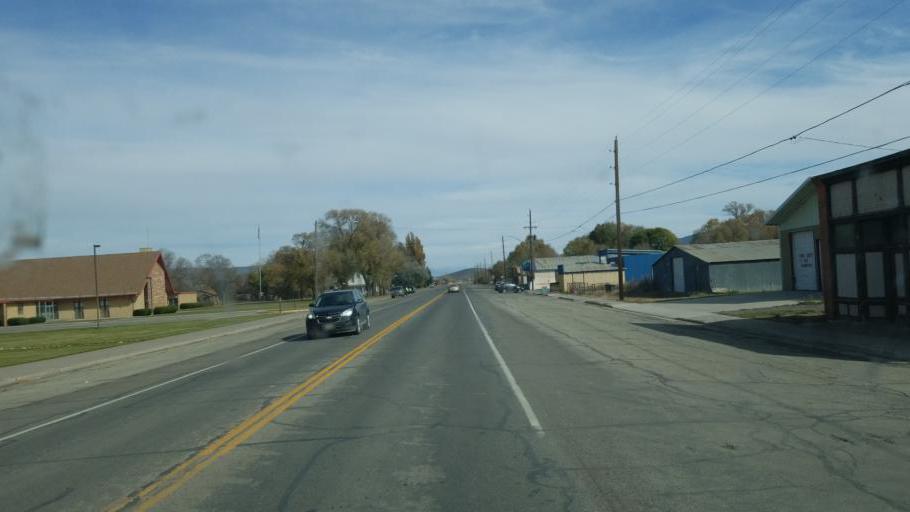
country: US
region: Colorado
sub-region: Conejos County
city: Conejos
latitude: 37.1738
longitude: -105.9351
